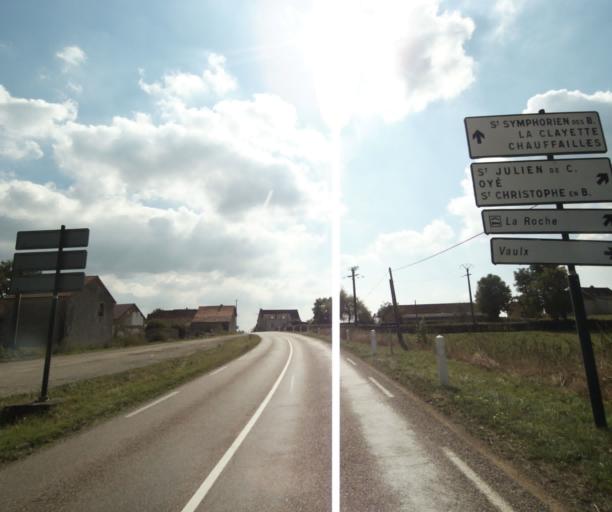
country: FR
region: Bourgogne
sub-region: Departement de Saone-et-Loire
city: Charolles
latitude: 46.3802
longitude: 4.2494
